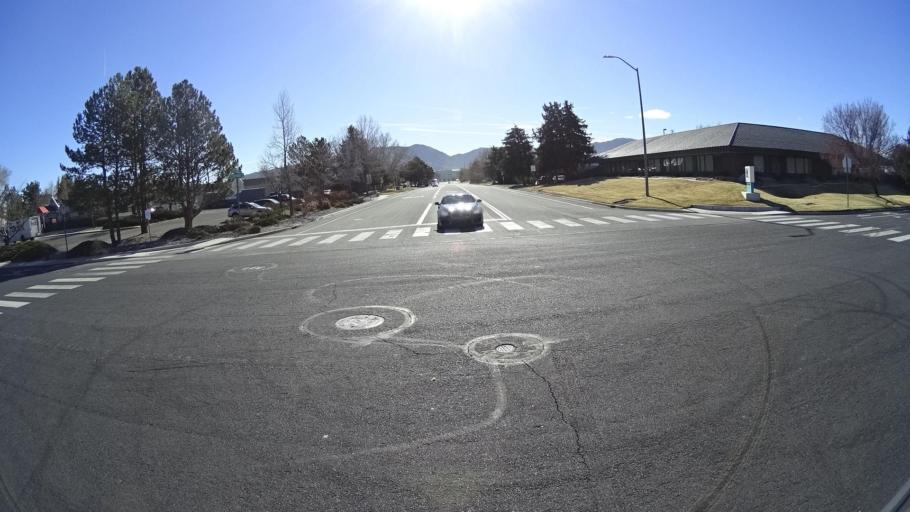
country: US
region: Nevada
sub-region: Washoe County
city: Sparks
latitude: 39.5106
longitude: -119.7507
